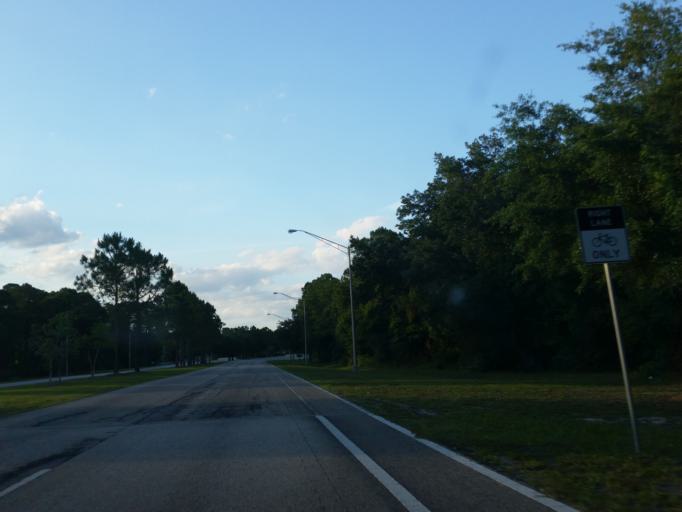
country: US
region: Florida
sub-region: Sarasota County
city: North Port
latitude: 27.0899
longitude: -82.2083
